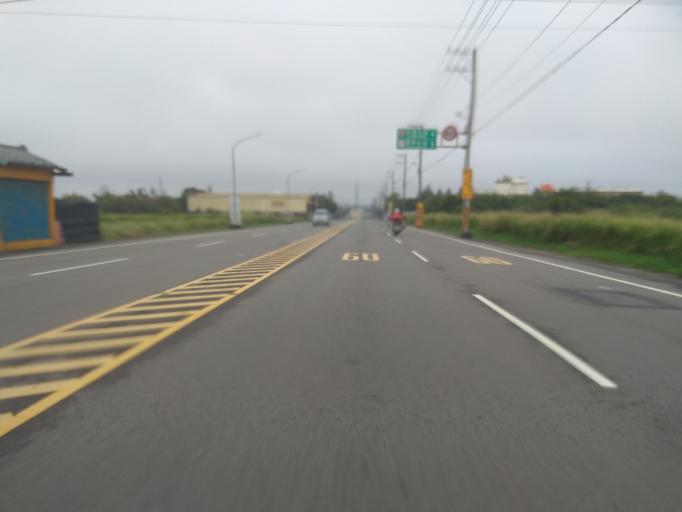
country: TW
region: Taiwan
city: Taoyuan City
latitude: 25.0162
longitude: 121.1290
